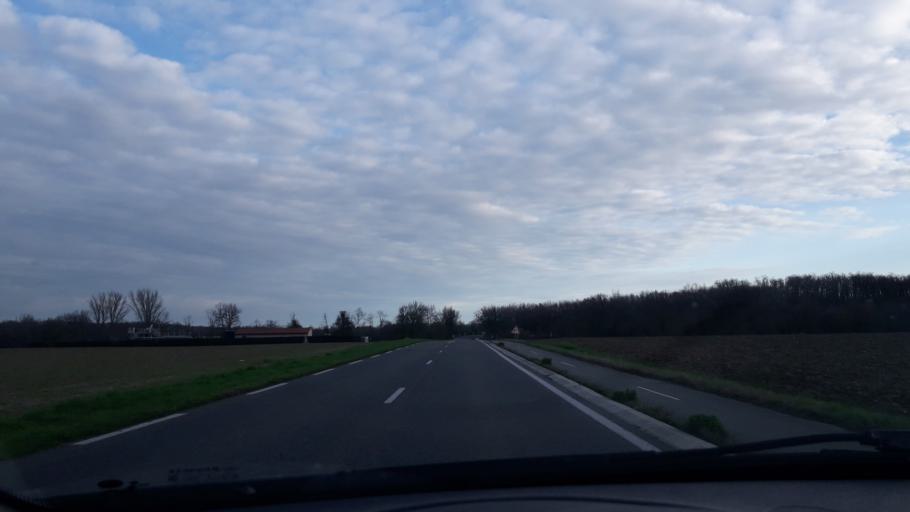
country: FR
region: Midi-Pyrenees
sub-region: Departement de la Haute-Garonne
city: Levignac
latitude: 43.6824
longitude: 1.2124
